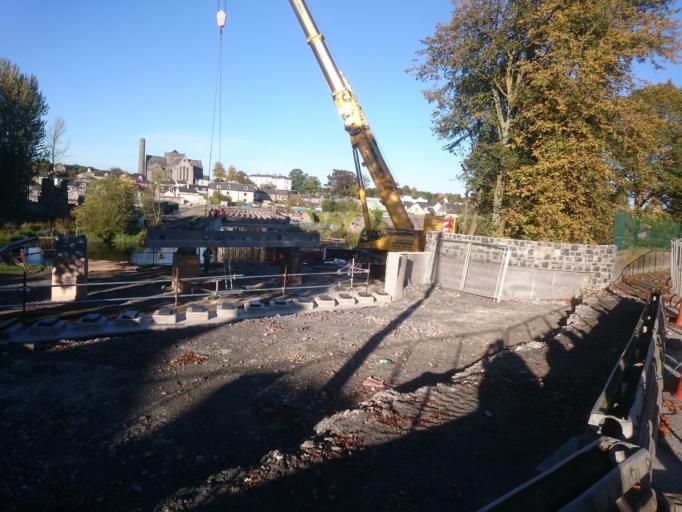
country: IE
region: Leinster
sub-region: Kilkenny
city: Kilkenny
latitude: 52.6569
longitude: -7.2516
